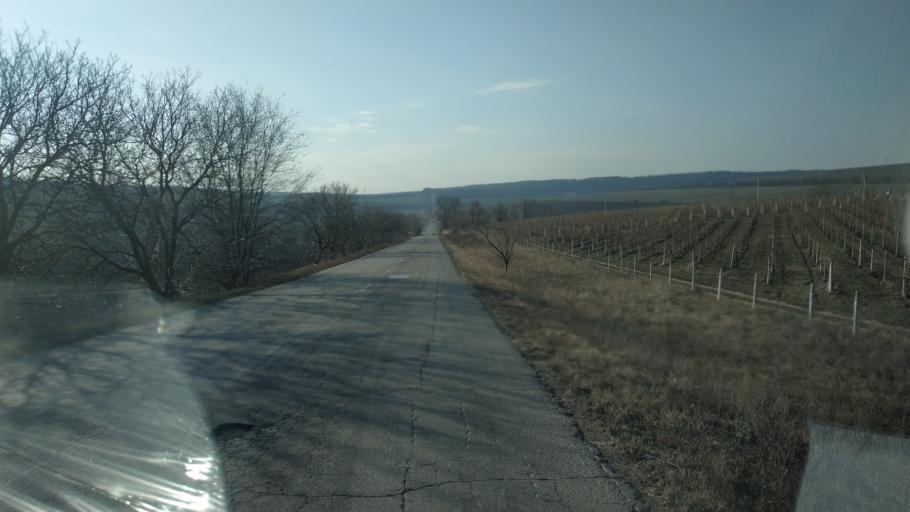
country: MD
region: Chisinau
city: Singera
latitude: 46.8908
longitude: 29.0391
